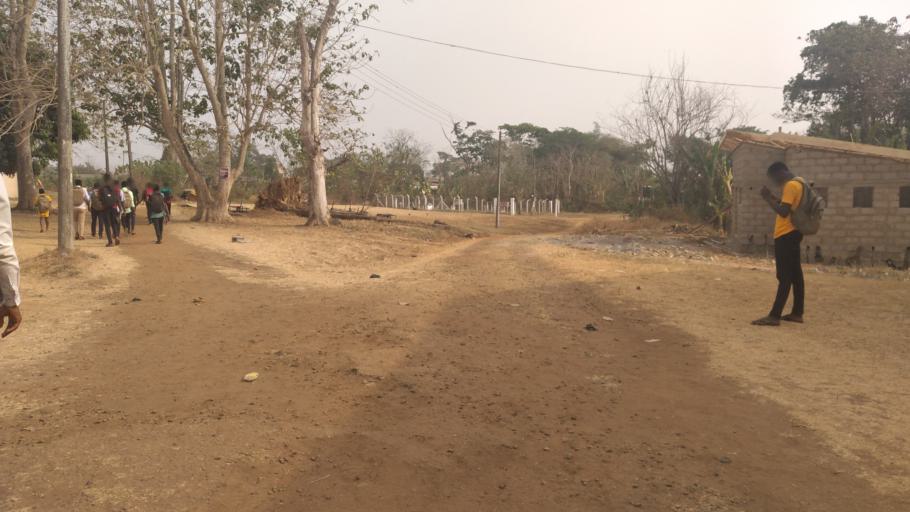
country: NG
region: Ondo
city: Akure
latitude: 7.2959
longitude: 5.1465
